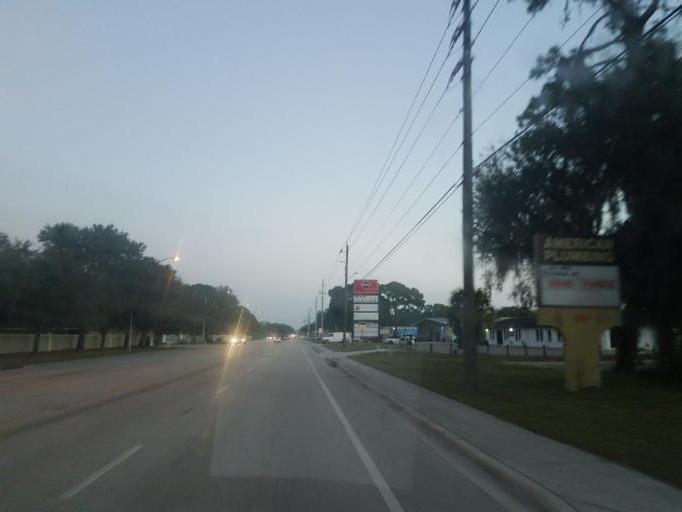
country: US
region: Florida
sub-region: Sarasota County
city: Fruitville
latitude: 27.3168
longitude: -82.4514
